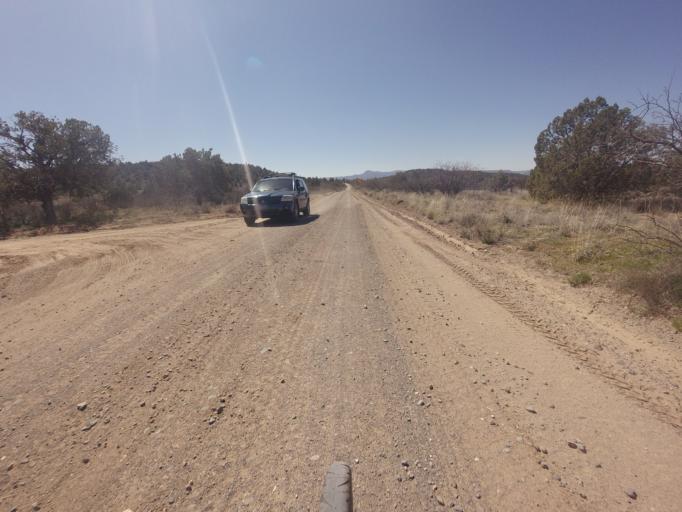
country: US
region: Arizona
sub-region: Yavapai County
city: Lake Montezuma
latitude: 34.5943
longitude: -111.7292
